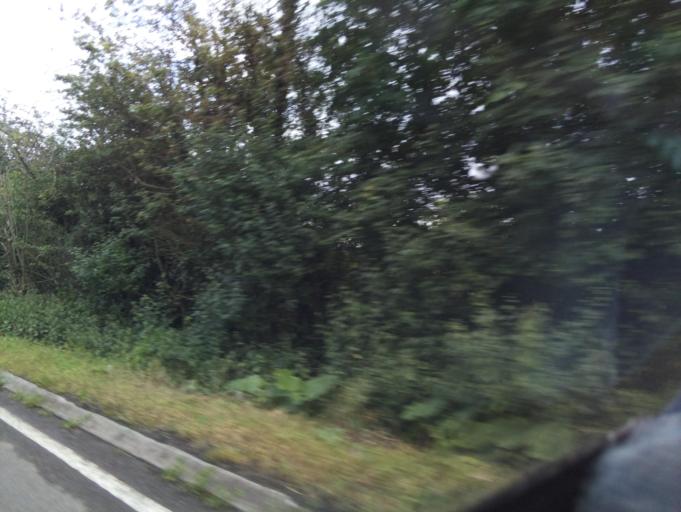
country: GB
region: England
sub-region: Warwickshire
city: Southam
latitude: 52.2644
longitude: -1.3830
